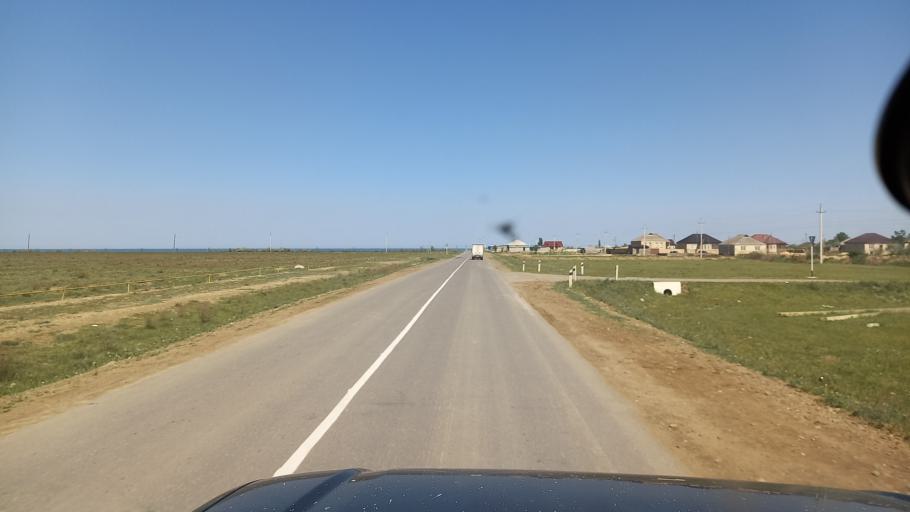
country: RU
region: Dagestan
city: Khazar
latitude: 41.9415
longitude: 48.3326
